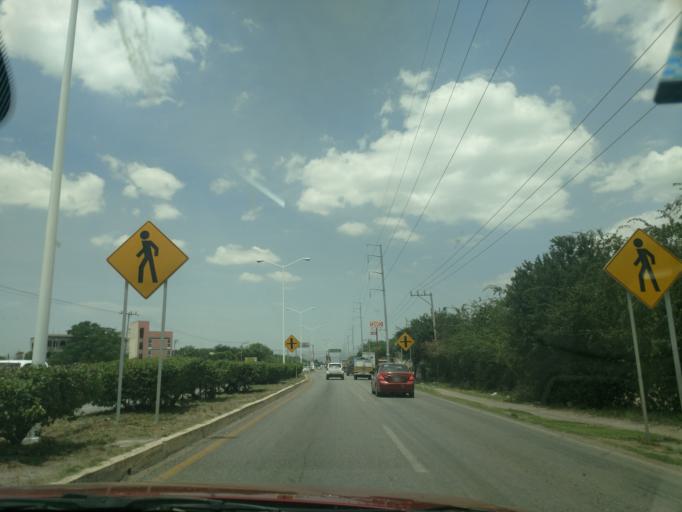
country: MX
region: San Luis Potosi
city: Rio Verde
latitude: 21.9225
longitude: -99.9825
